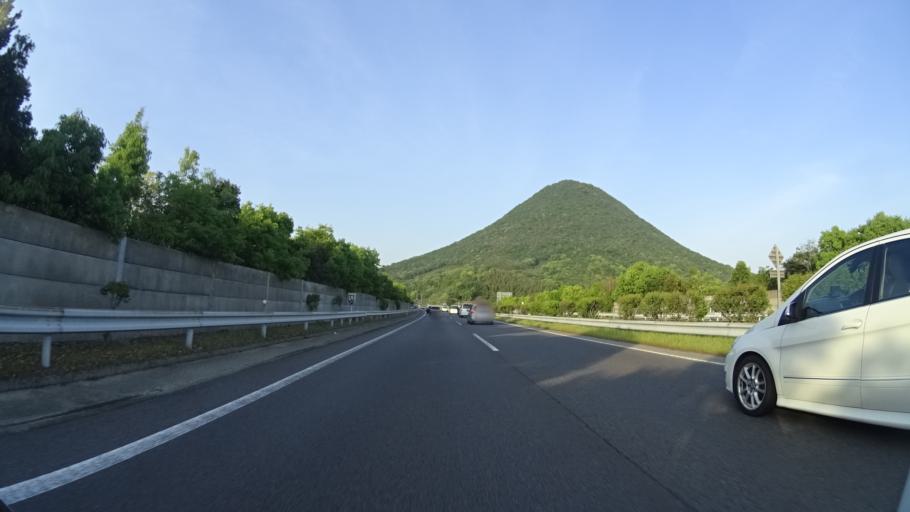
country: JP
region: Kagawa
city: Marugame
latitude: 34.2720
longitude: 133.8308
